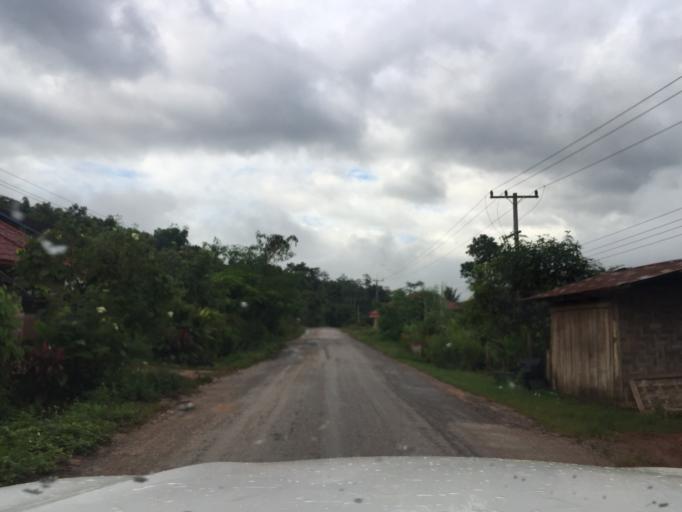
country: LA
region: Oudomxai
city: Muang La
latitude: 20.8528
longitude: 102.1092
